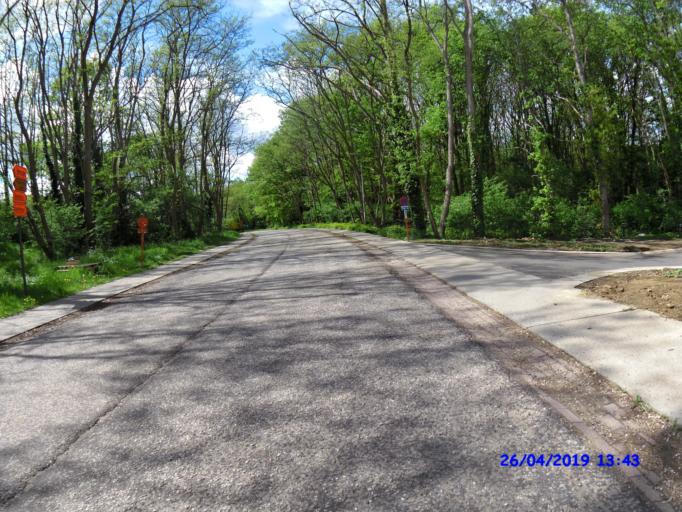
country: BE
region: Flanders
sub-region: Provincie Limburg
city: Heusden
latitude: 51.0379
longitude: 5.2929
